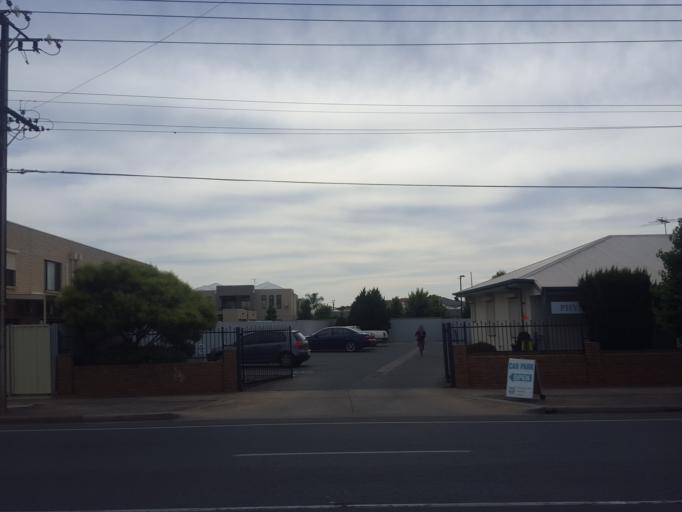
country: AU
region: South Australia
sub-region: Charles Sturt
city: Woodville North
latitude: -34.8570
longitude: 138.5472
